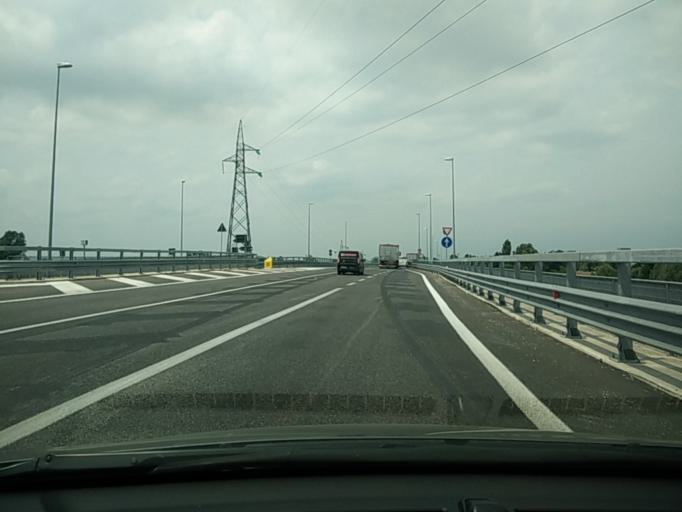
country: IT
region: Veneto
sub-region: Provincia di Venezia
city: Portogruaro
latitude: 45.7858
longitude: 12.8431
